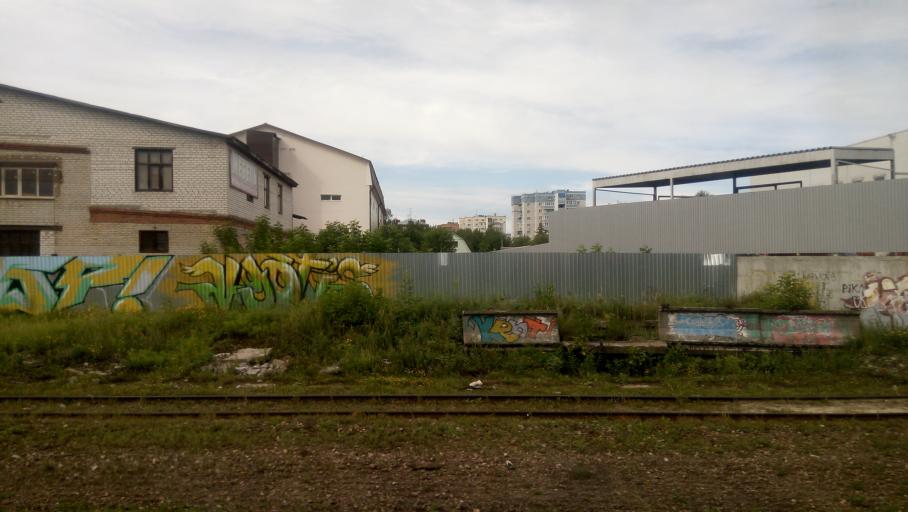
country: RU
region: Moskovskaya
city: Pavlovskiy Posad
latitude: 55.7758
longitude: 38.6635
